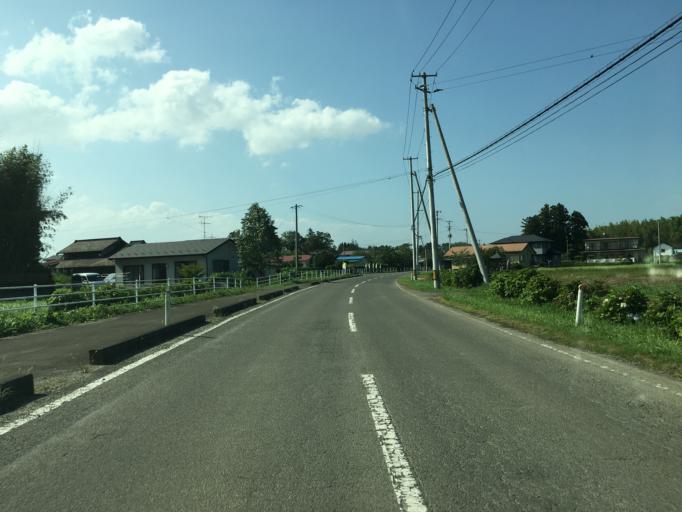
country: JP
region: Miyagi
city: Kakuda
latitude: 37.9482
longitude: 140.7971
